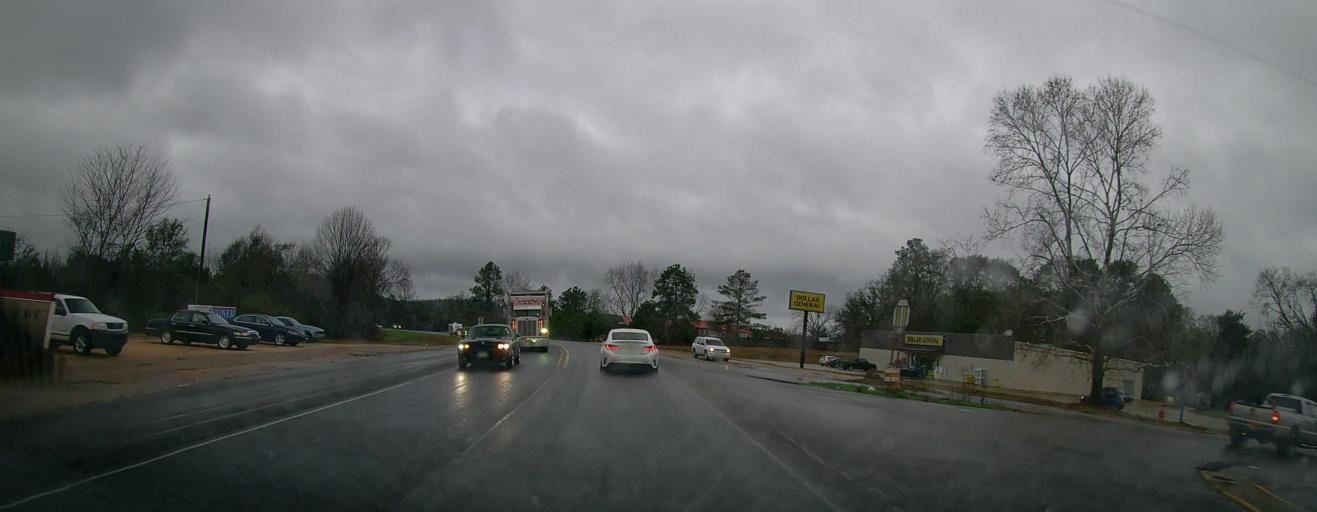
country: US
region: Alabama
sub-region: Chilton County
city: Clanton
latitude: 32.6282
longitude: -86.7385
